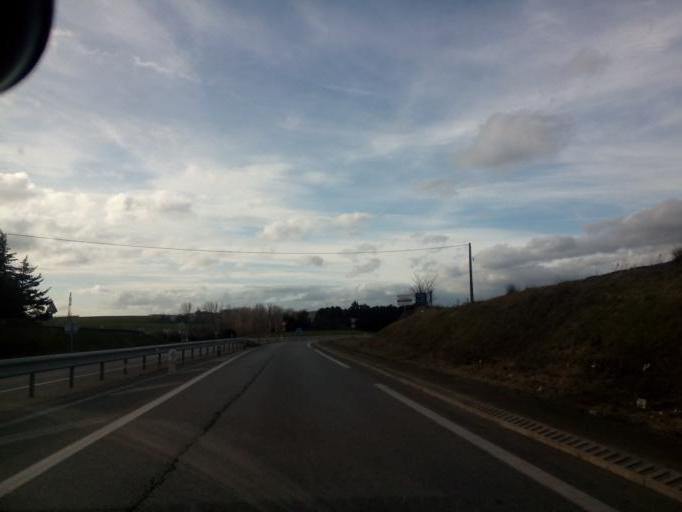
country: FR
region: Rhone-Alpes
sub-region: Departement de l'Ardeche
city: Peaugres
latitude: 45.2923
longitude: 4.7354
